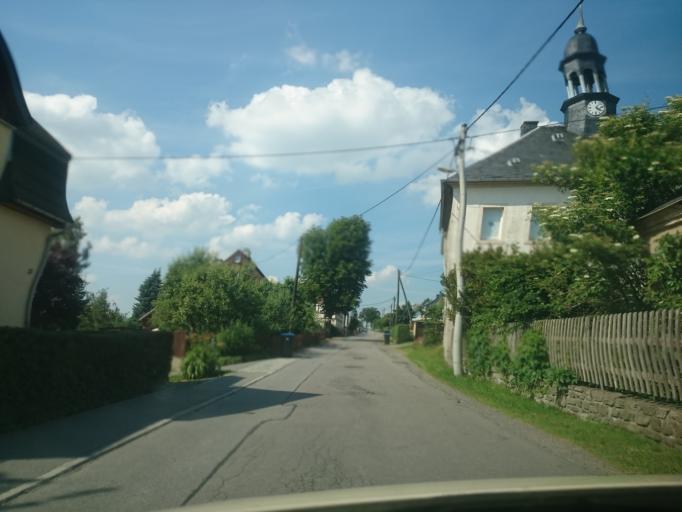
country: DE
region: Saxony
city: Lengefeld
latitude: 50.7398
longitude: 13.2105
